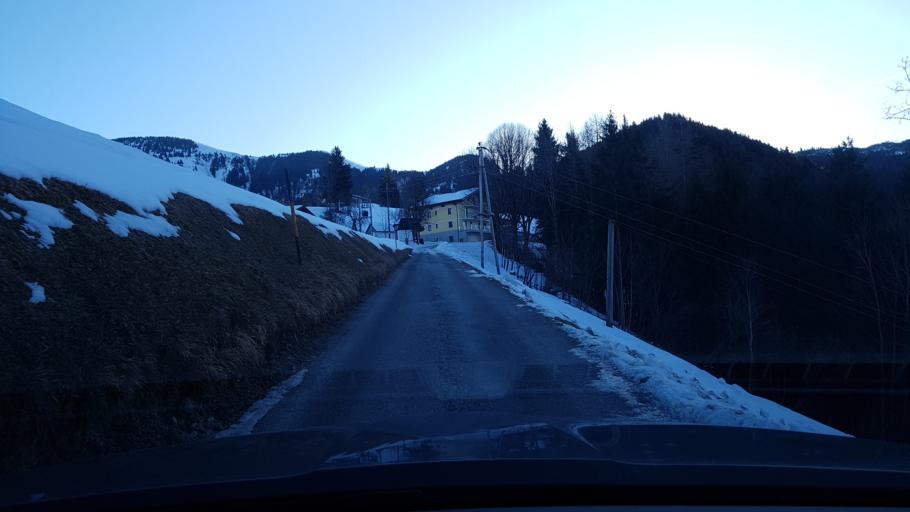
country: AT
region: Salzburg
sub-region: Politischer Bezirk Hallein
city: Scheffau am Tennengebirge
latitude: 47.6478
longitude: 13.2346
